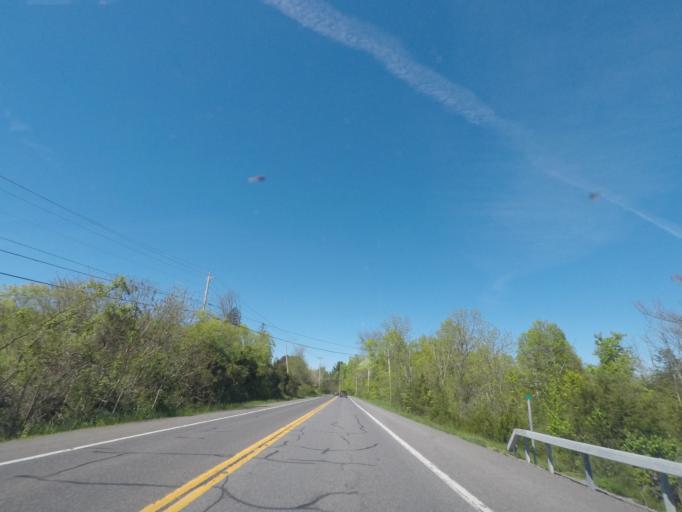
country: US
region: New York
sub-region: Ulster County
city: Saugerties
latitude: 42.1100
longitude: -73.9367
